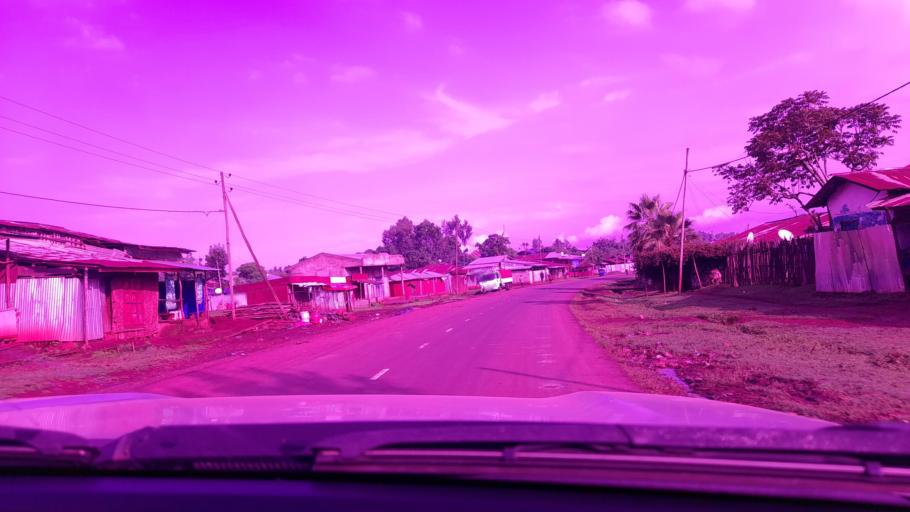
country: ET
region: Oromiya
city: Bedele
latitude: 8.1718
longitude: 36.4610
